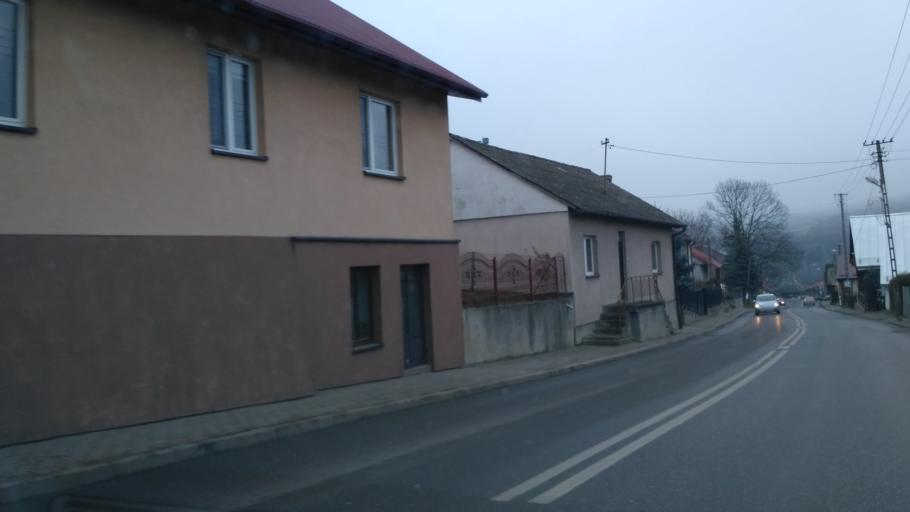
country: PL
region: Subcarpathian Voivodeship
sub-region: Powiat jaroslawski
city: Pruchnik
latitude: 49.9076
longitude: 22.5138
